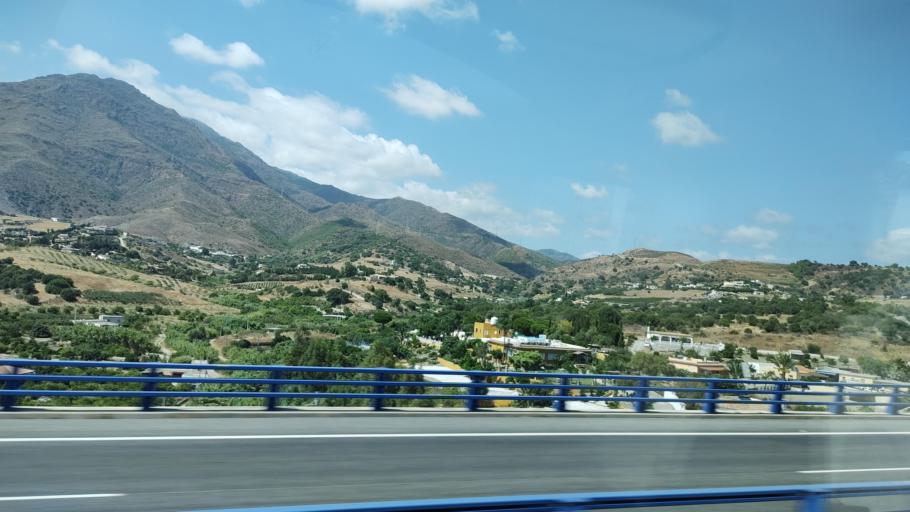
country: ES
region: Andalusia
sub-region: Provincia de Malaga
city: Estepona
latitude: 36.4333
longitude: -5.1829
